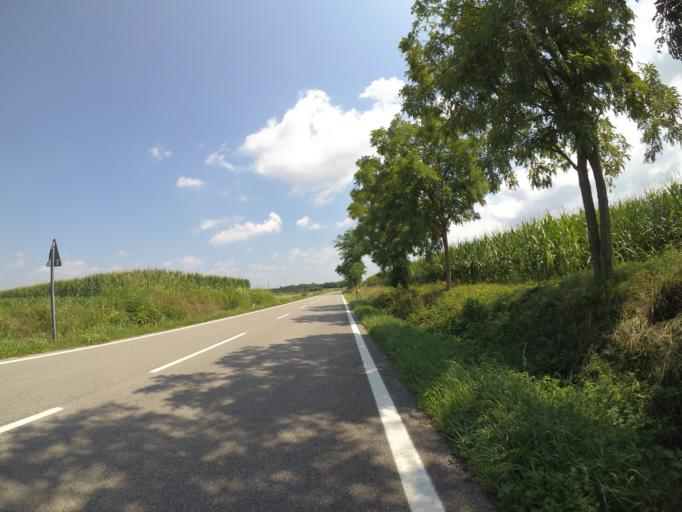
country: IT
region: Friuli Venezia Giulia
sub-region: Provincia di Udine
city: Sedegliano
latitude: 46.0179
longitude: 12.9972
